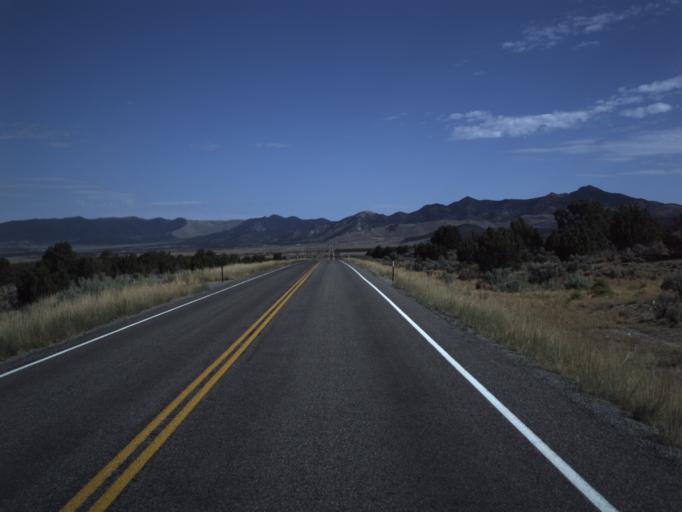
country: US
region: Utah
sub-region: Juab County
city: Mona
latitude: 39.8394
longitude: -112.1381
